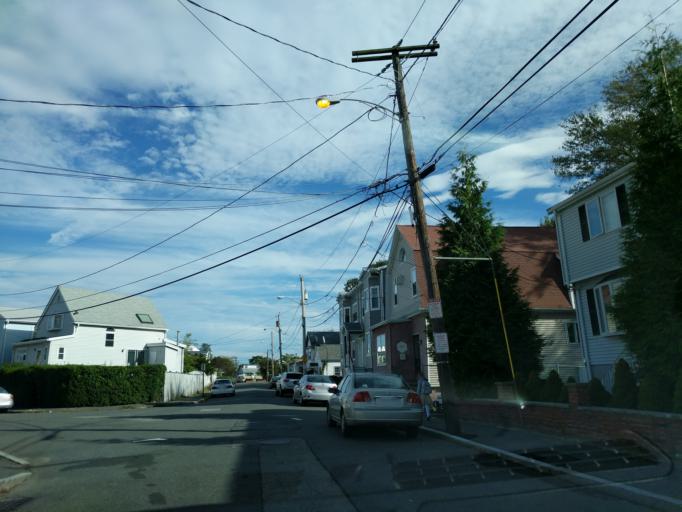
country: US
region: Massachusetts
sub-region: Suffolk County
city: Winthrop
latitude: 42.3993
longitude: -70.9888
